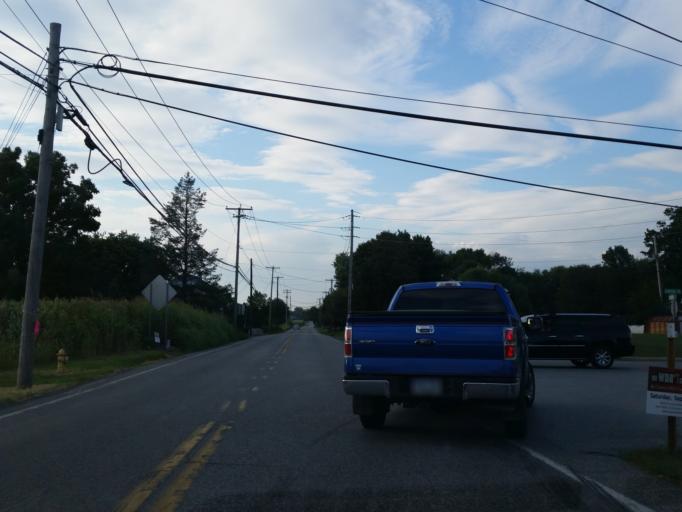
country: US
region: Pennsylvania
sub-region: Lebanon County
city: Campbelltown
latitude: 40.2884
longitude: -76.5745
